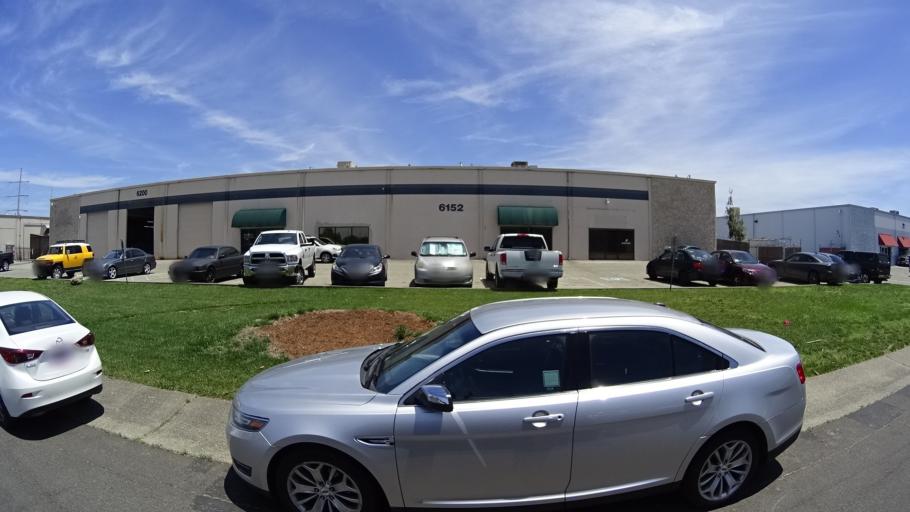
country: US
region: California
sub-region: Sacramento County
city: Rosemont
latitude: 38.5312
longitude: -121.3825
